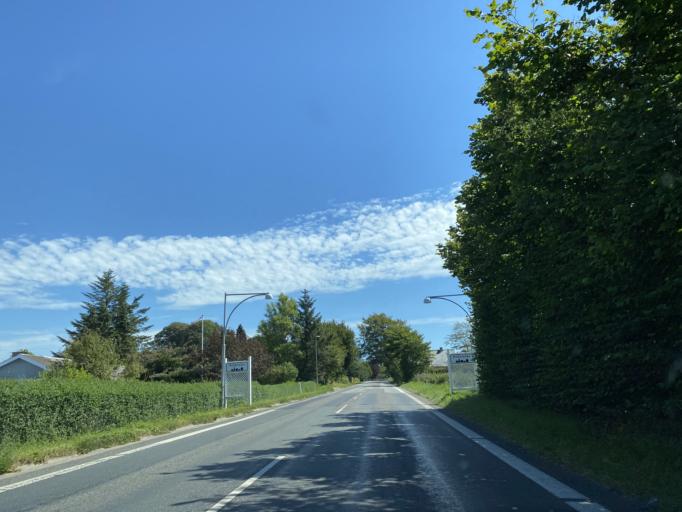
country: DK
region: South Denmark
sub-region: Odense Kommune
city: Bellinge
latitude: 55.2091
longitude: 10.3398
